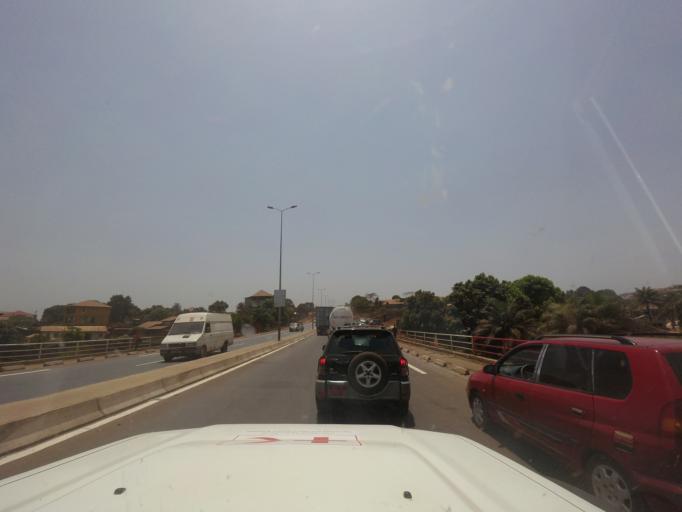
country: GN
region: Kindia
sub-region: Prefecture de Dubreka
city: Dubreka
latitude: 9.6980
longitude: -13.5017
